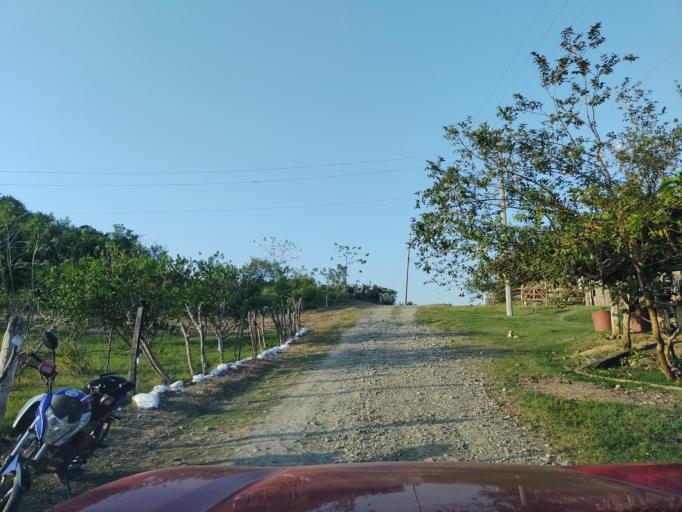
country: MX
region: Veracruz
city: Agua Dulce
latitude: 20.2870
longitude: -97.2468
